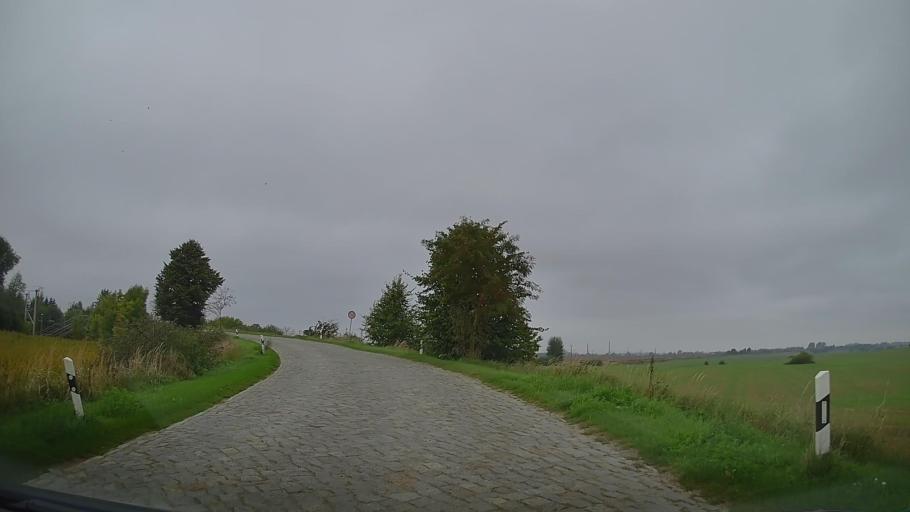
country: DE
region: Mecklenburg-Vorpommern
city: Dummerstorf
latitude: 53.9706
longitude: 12.2470
